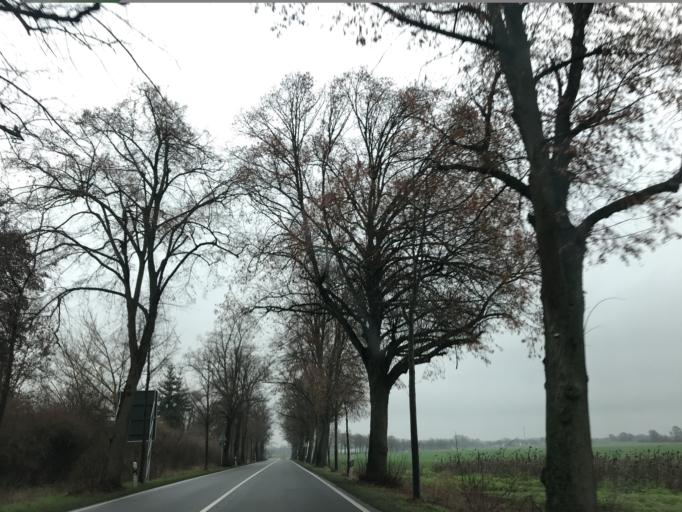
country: DE
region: Brandenburg
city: Kremmen
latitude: 52.7500
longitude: 13.0084
